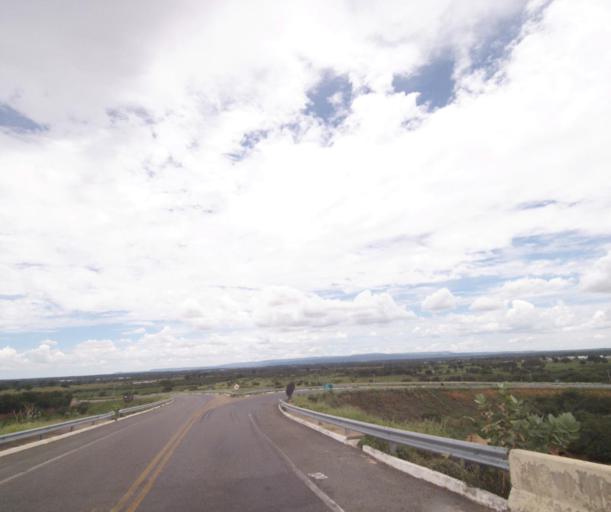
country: BR
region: Bahia
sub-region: Carinhanha
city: Carinhanha
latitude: -14.3268
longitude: -43.7655
